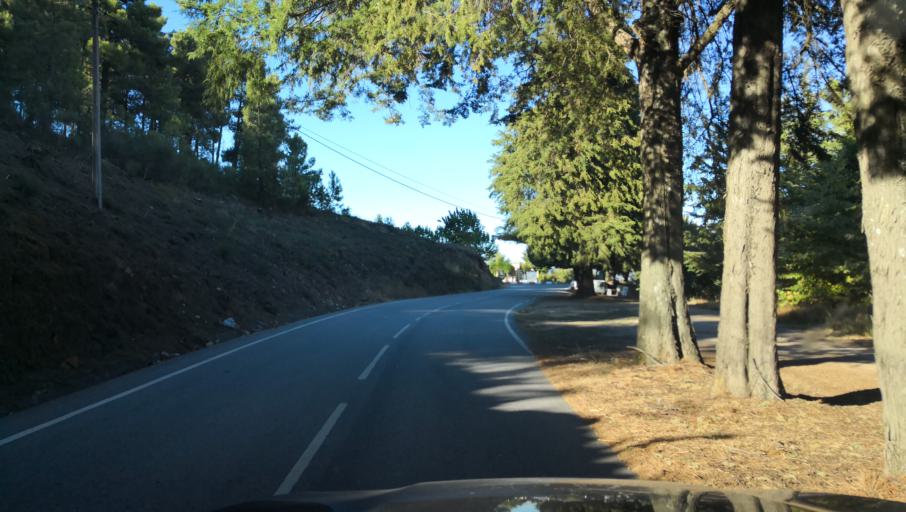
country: PT
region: Vila Real
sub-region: Sabrosa
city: Sabrosa
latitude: 41.2731
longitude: -7.5682
